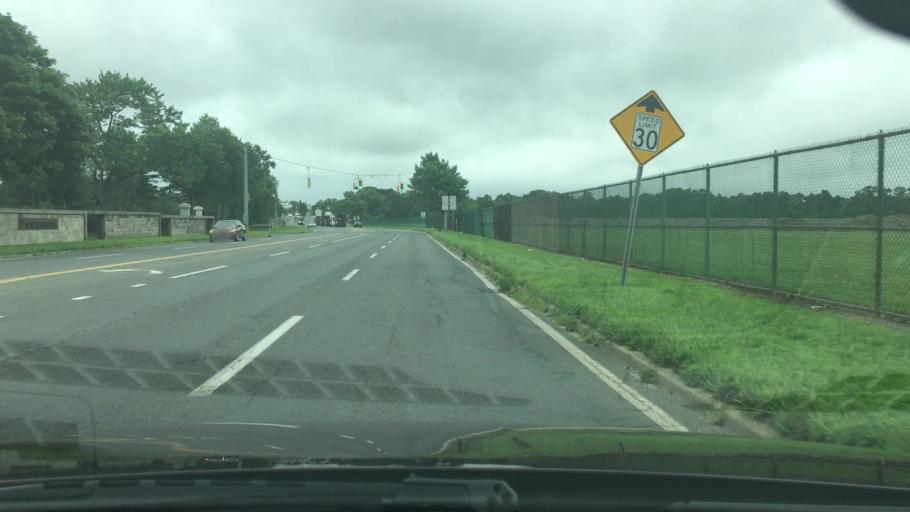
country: US
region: New York
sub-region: Suffolk County
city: North Lindenhurst
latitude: 40.7253
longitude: -73.3963
